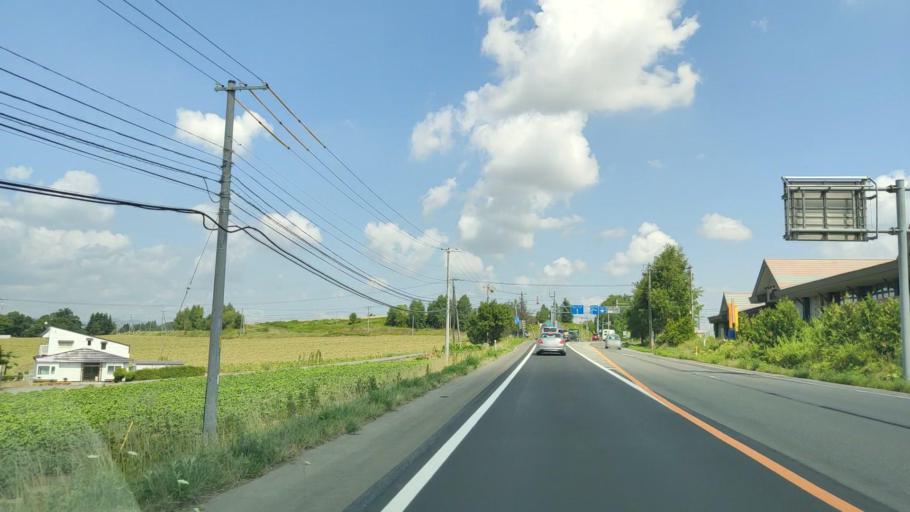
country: JP
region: Hokkaido
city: Shimo-furano
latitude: 43.5438
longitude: 142.4386
